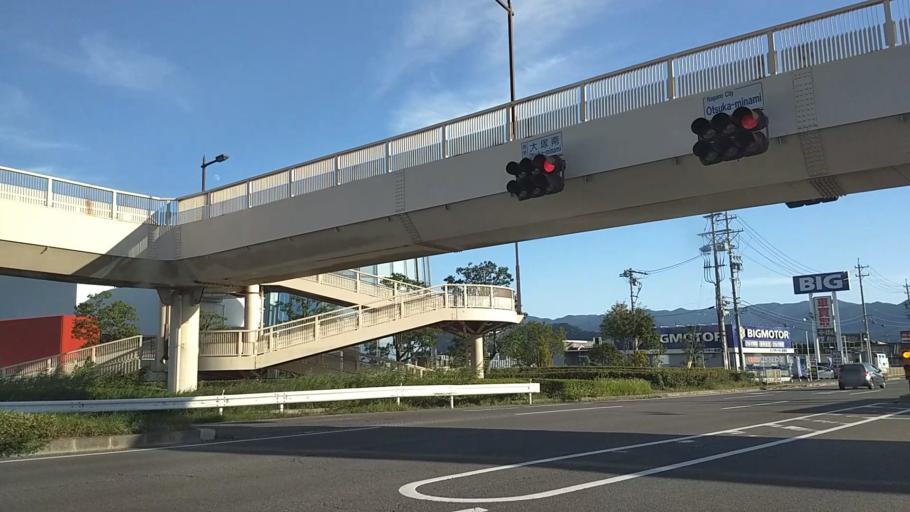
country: JP
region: Nagano
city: Nagano-shi
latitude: 36.6054
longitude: 138.1950
